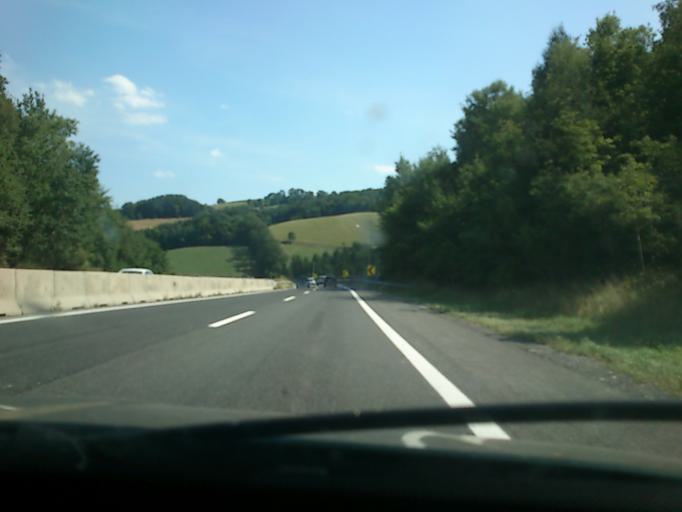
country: AT
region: Lower Austria
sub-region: Politischer Bezirk Neunkirchen
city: Grimmenstein
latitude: 47.6020
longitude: 16.1268
